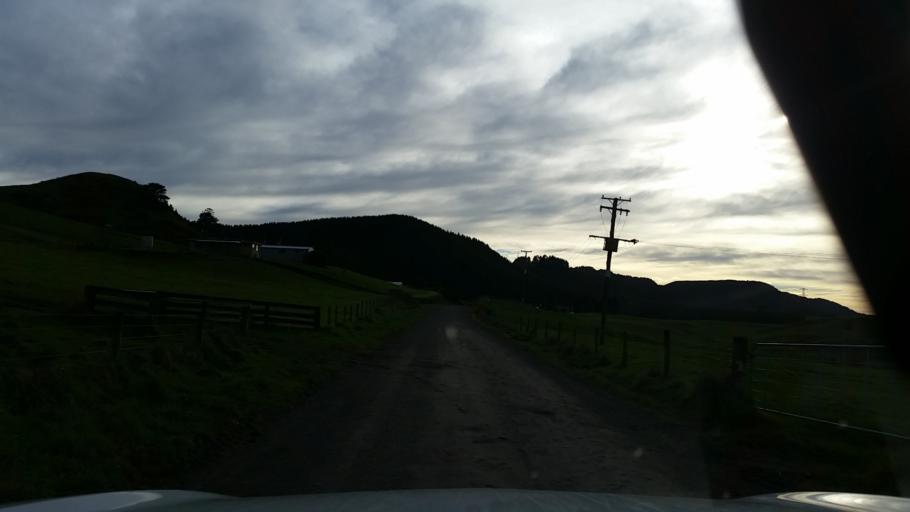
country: NZ
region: Bay of Plenty
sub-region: Rotorua District
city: Rotorua
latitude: -38.2316
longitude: 176.1586
